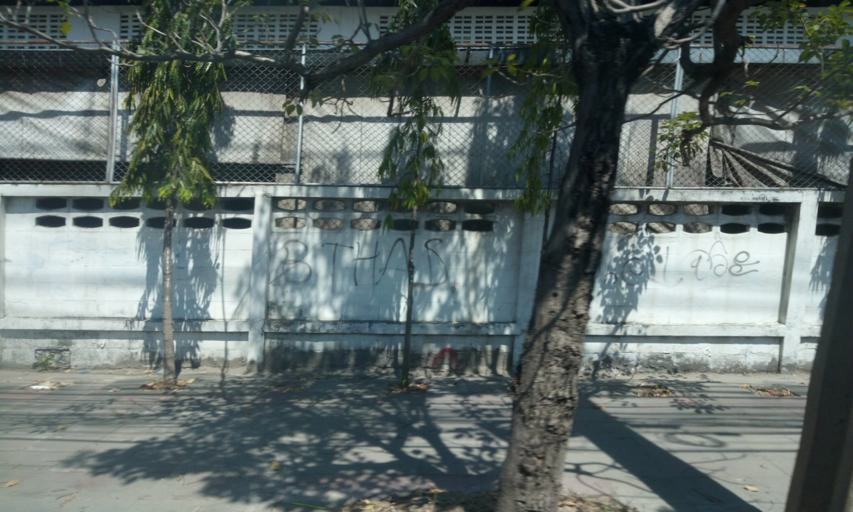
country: TH
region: Samut Prakan
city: Bang Bo District
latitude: 13.5806
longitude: 100.7961
